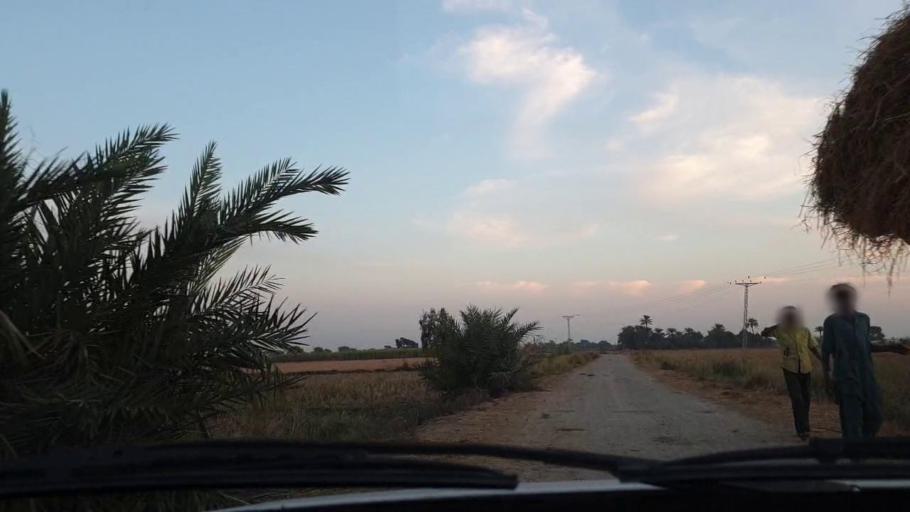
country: PK
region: Sindh
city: Tando Muhammad Khan
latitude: 25.0909
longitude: 68.3938
